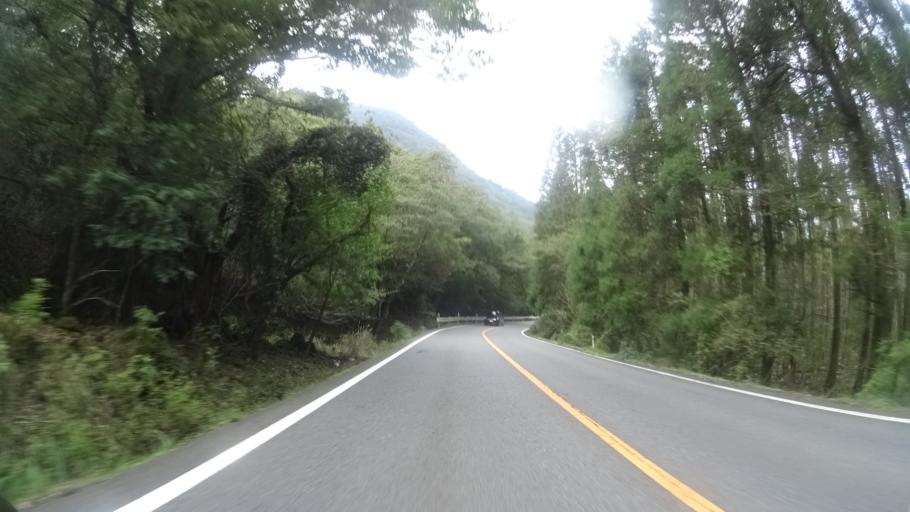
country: JP
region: Oita
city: Beppu
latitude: 33.2695
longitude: 131.4079
